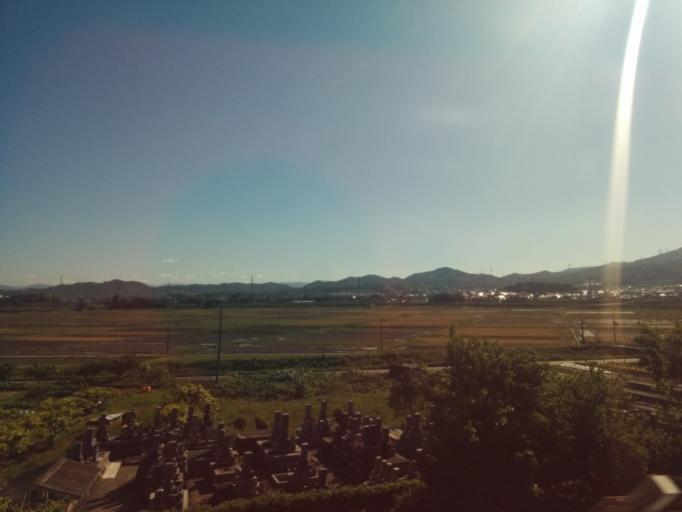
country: JP
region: Aichi
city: Okazaki
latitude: 34.8697
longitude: 137.1519
